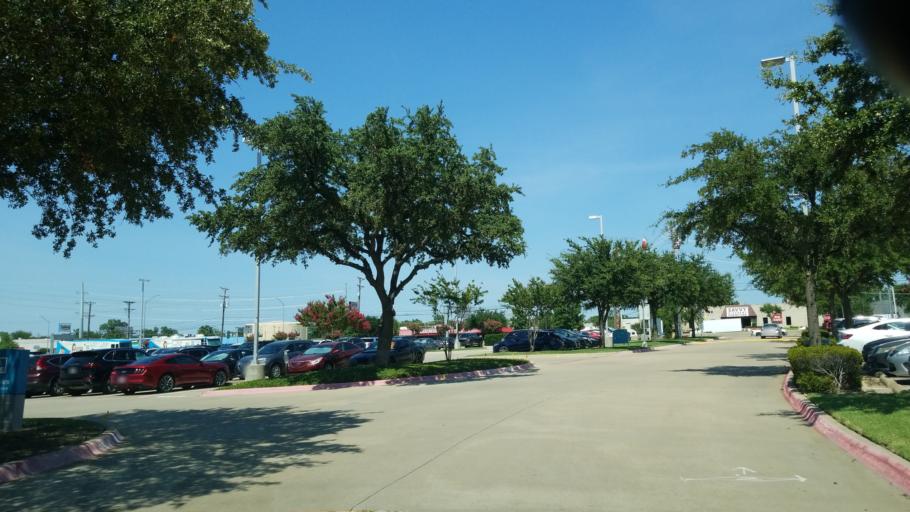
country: US
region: Texas
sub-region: Dallas County
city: Farmers Branch
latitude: 32.9295
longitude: -96.9031
